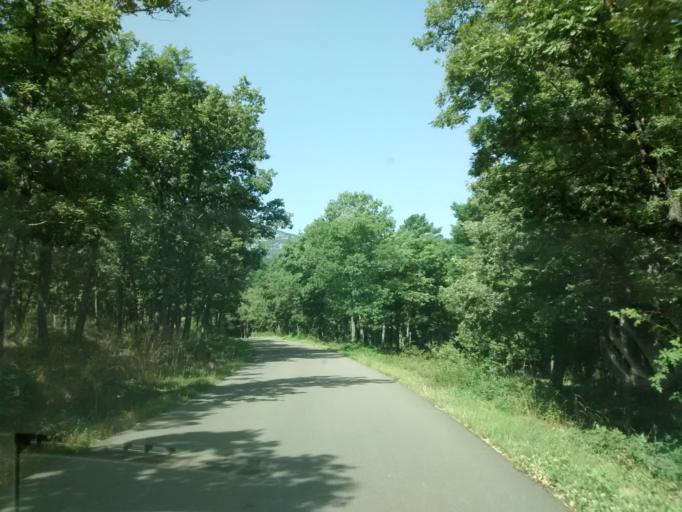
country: ES
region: Aragon
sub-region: Provincia de Zaragoza
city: Lituenigo
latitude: 41.8104
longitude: -1.8074
